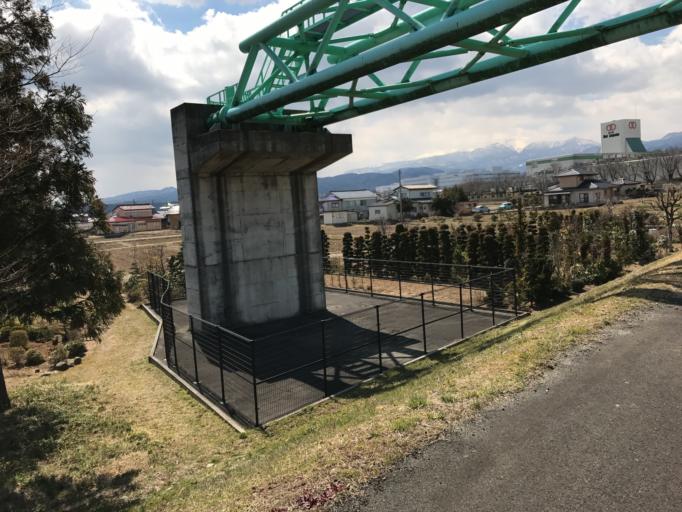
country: JP
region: Fukushima
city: Fukushima-shi
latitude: 37.7478
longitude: 140.4097
